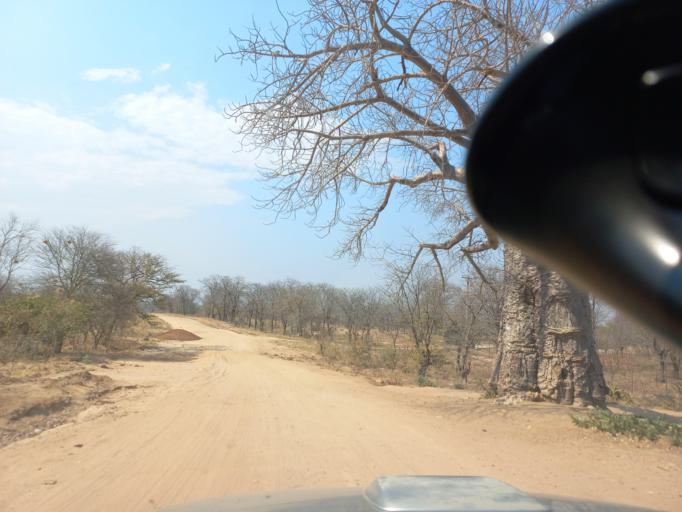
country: ZW
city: Chirundu
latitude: -15.9375
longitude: 28.9143
